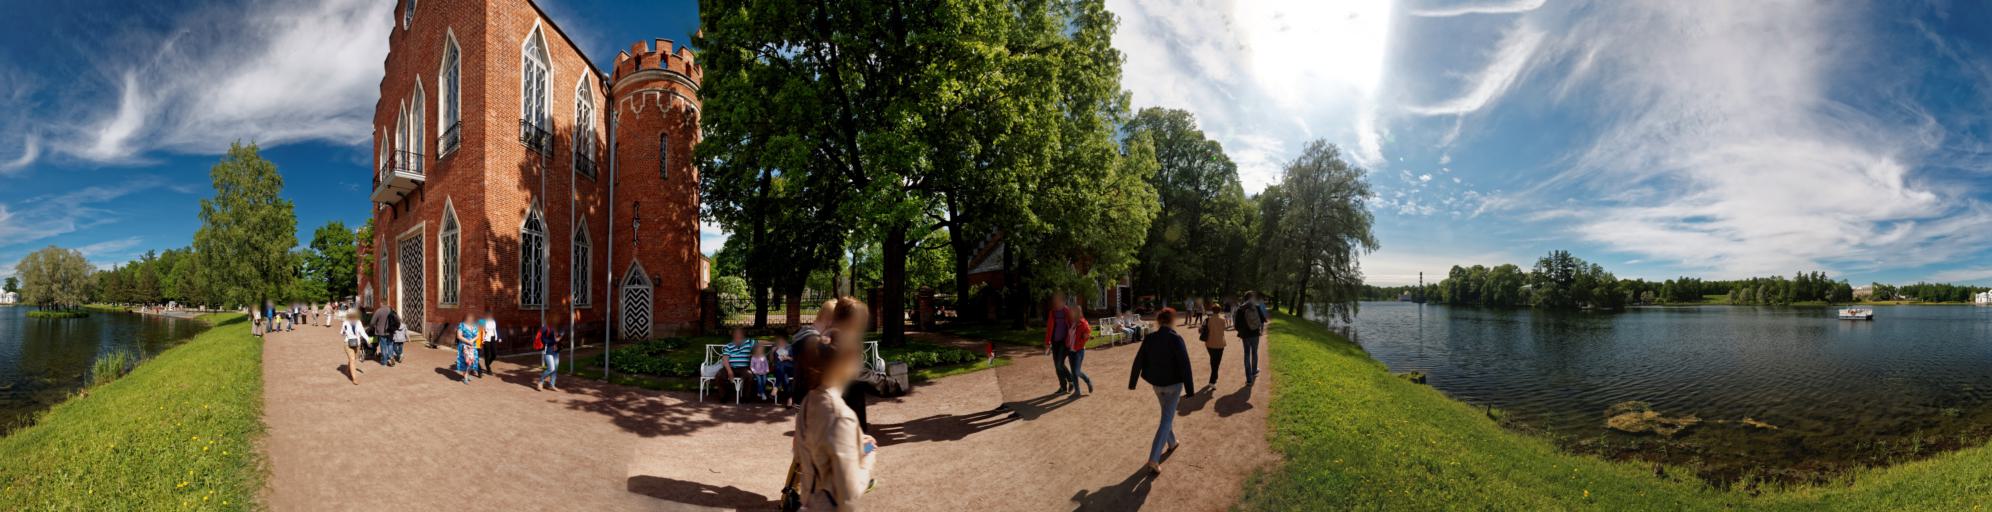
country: RU
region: St.-Petersburg
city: Pushkin
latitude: 59.7098
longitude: 30.3983
